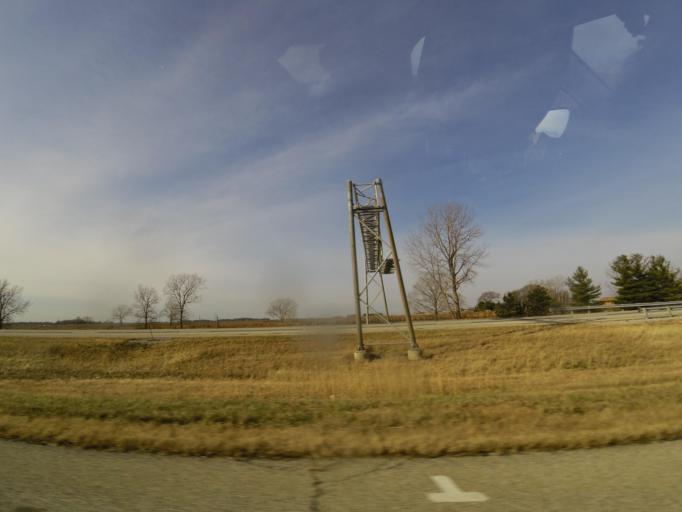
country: US
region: Illinois
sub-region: Macon County
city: Harristown
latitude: 39.8585
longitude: -89.0453
